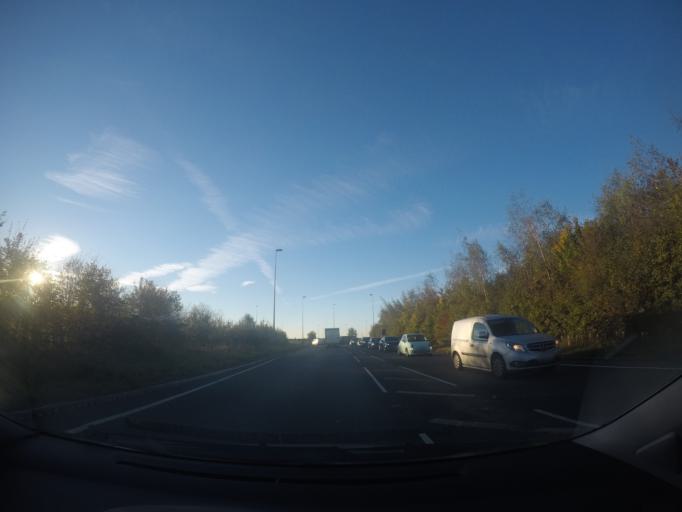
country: GB
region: England
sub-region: City of York
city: Copmanthorpe
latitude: 53.9374
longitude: -1.1448
